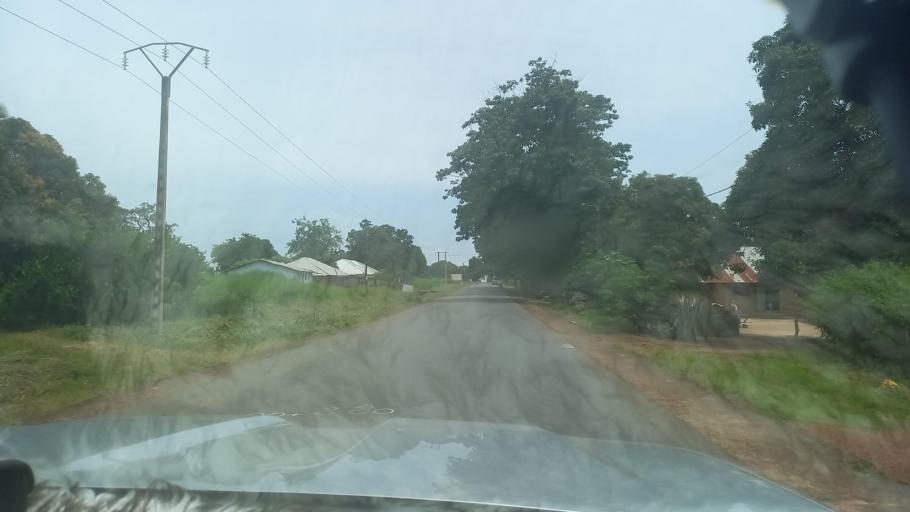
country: SN
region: Kolda
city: Marsassoum
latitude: 12.9603
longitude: -15.9934
